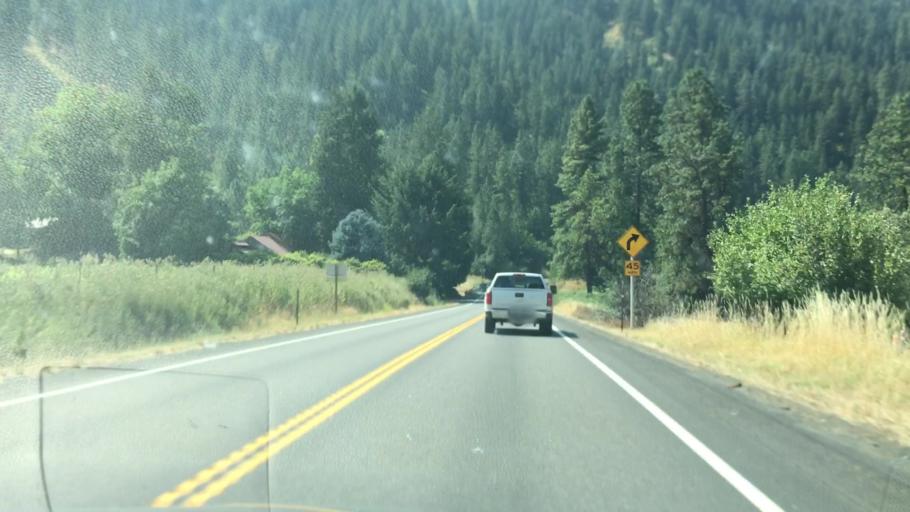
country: US
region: Idaho
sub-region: Clearwater County
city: Orofino
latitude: 46.4928
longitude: -116.4494
